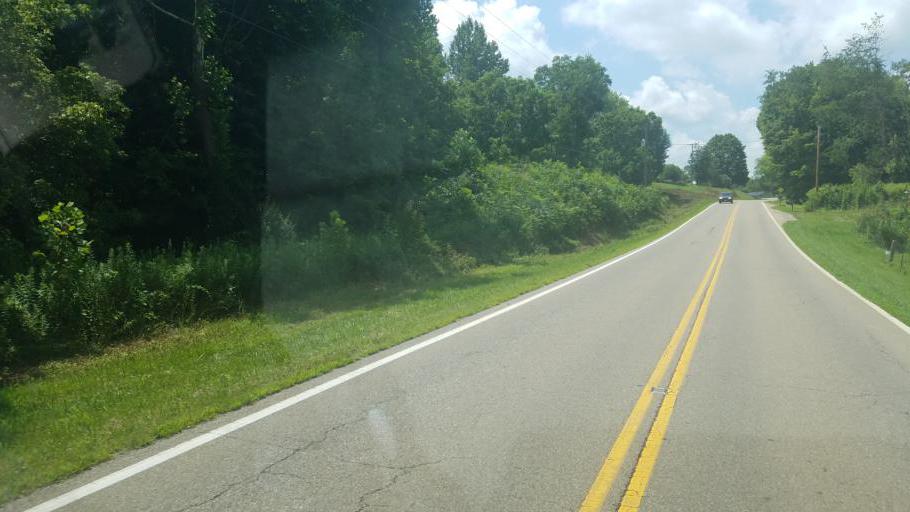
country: US
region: Ohio
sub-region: Ross County
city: Chillicothe
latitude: 39.2715
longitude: -82.7877
